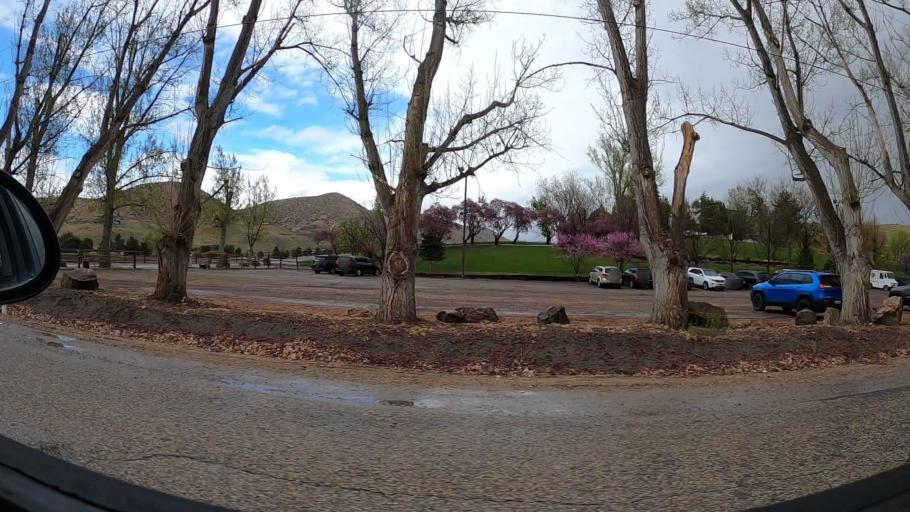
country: US
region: Idaho
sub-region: Ada County
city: Eagle
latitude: 43.7356
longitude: -116.3001
